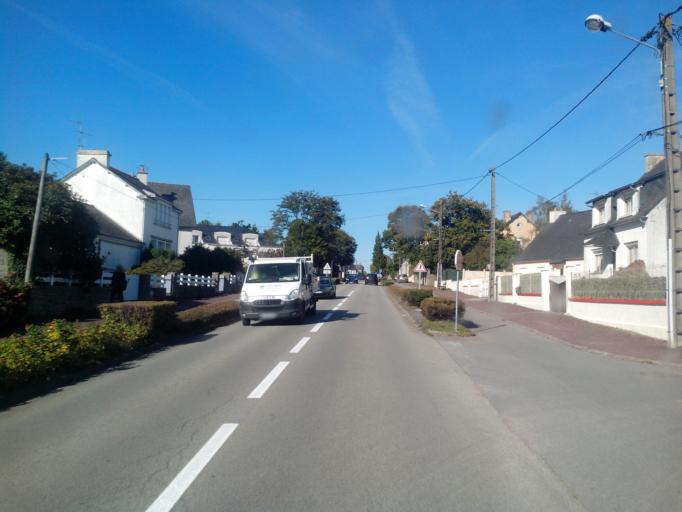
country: FR
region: Brittany
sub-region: Departement du Morbihan
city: Ploermel
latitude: 47.9249
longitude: -2.4012
